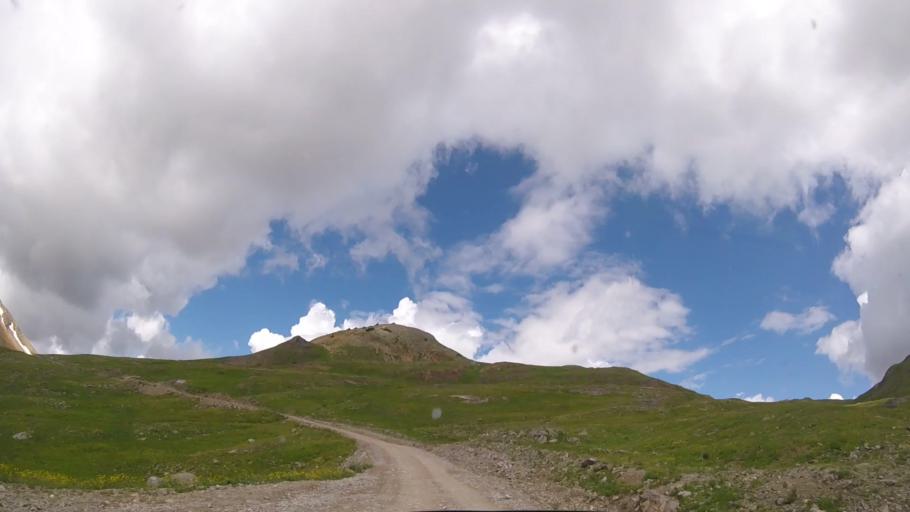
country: US
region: Colorado
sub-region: Ouray County
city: Ouray
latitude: 37.9503
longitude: -107.5733
